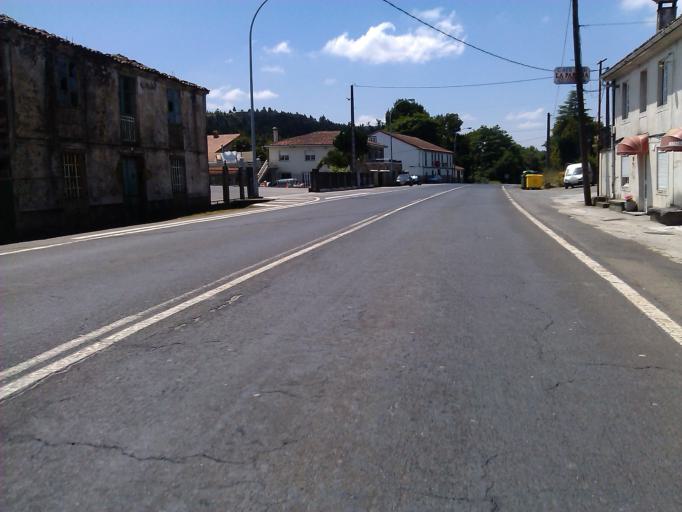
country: ES
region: Galicia
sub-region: Provincia da Coruna
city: Oroso
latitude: 42.8993
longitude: -8.4430
